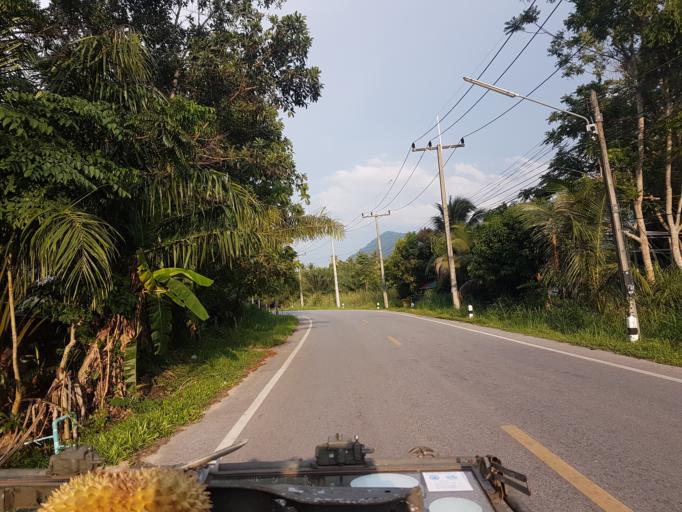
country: TH
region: Pattani
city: Khok Pho
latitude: 6.6752
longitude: 101.0969
